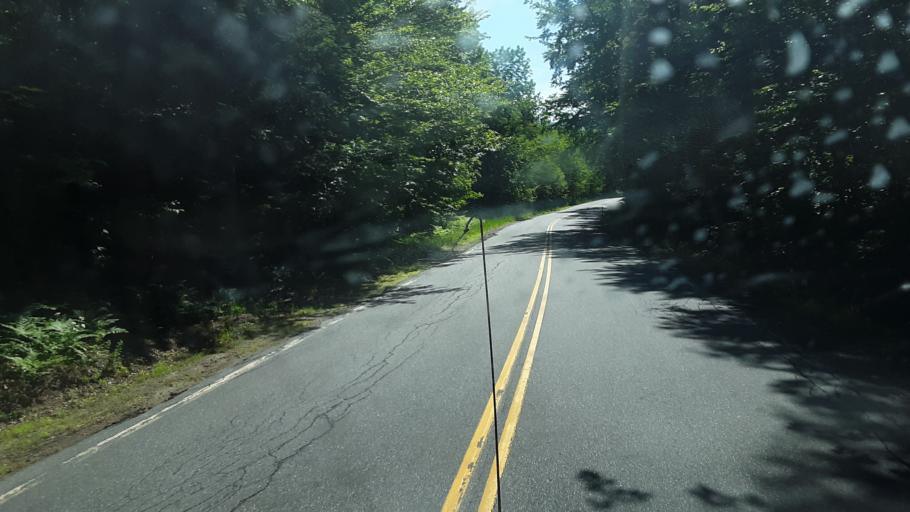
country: US
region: New Hampshire
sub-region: Grafton County
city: North Haverhill
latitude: 44.0982
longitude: -71.8662
